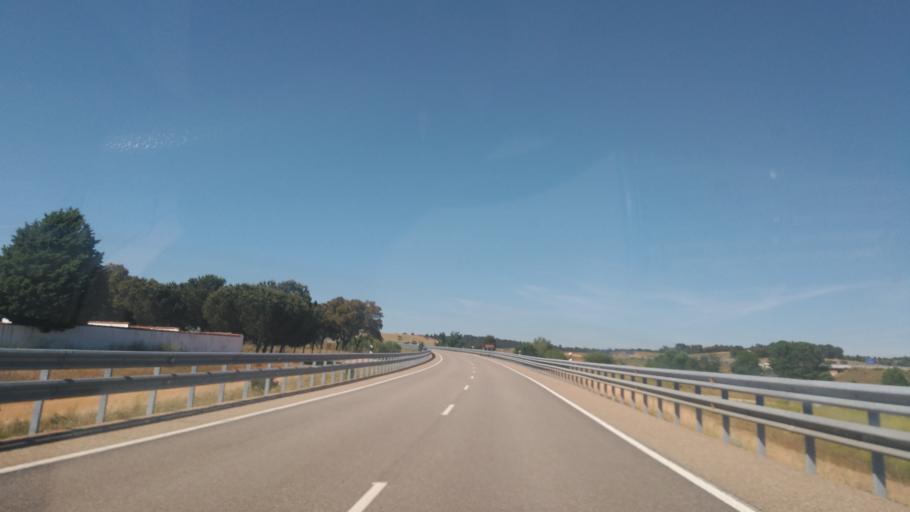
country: ES
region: Castille and Leon
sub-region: Provincia de Zamora
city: Cuelgamures
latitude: 41.2504
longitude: -5.7045
